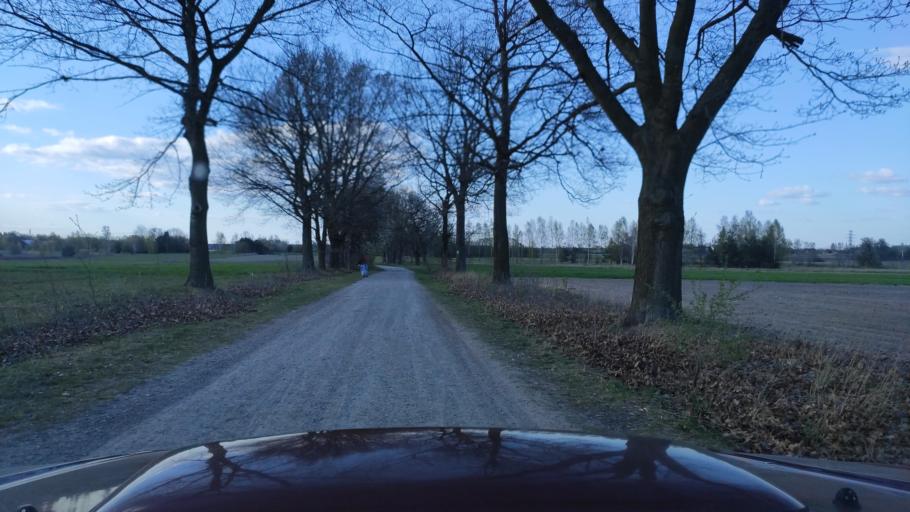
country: PL
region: Masovian Voivodeship
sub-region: Powiat zwolenski
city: Zwolen
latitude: 51.3643
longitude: 21.5758
